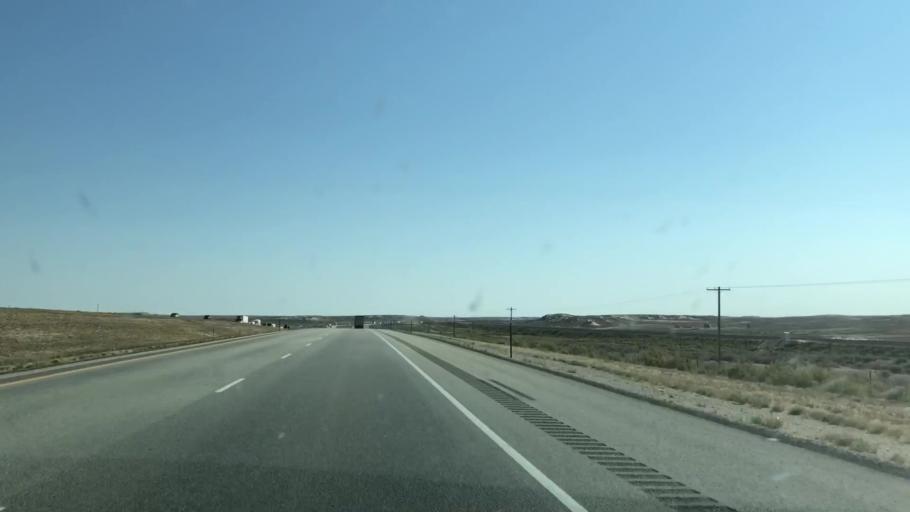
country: US
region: Wyoming
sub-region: Carbon County
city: Rawlins
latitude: 41.6978
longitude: -107.9179
